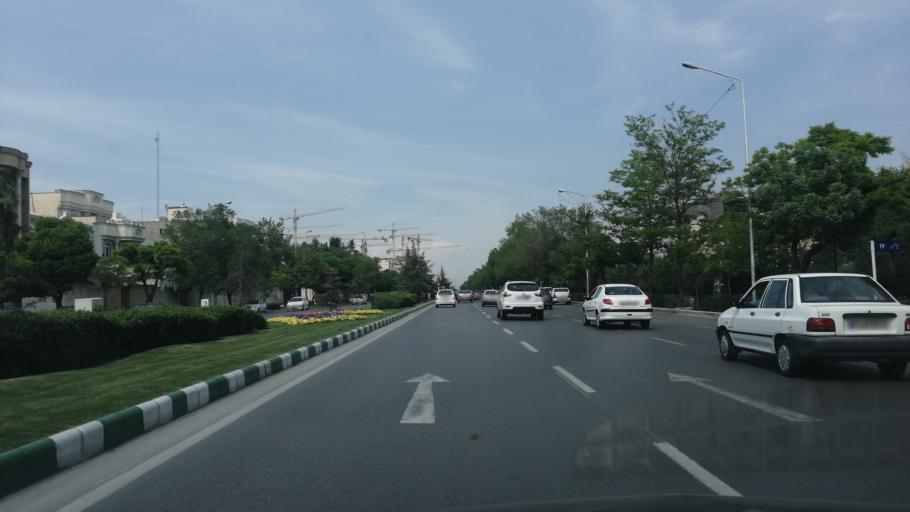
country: IR
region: Razavi Khorasan
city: Mashhad
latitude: 36.3110
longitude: 59.5562
